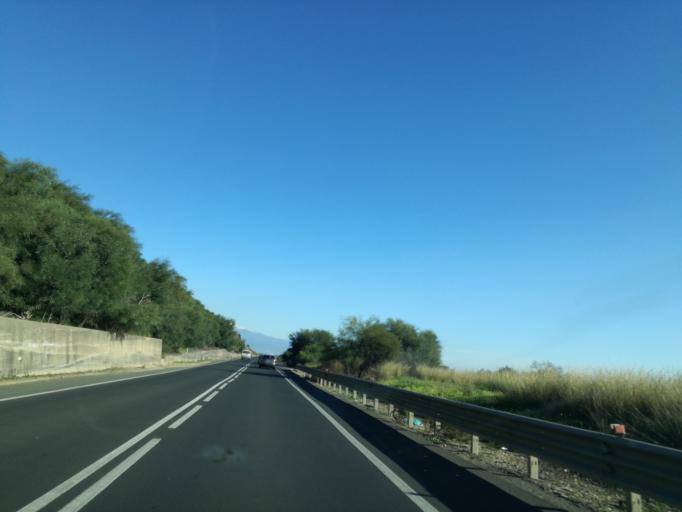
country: IT
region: Sicily
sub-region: Catania
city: Ramacca
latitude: 37.3658
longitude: 14.7196
